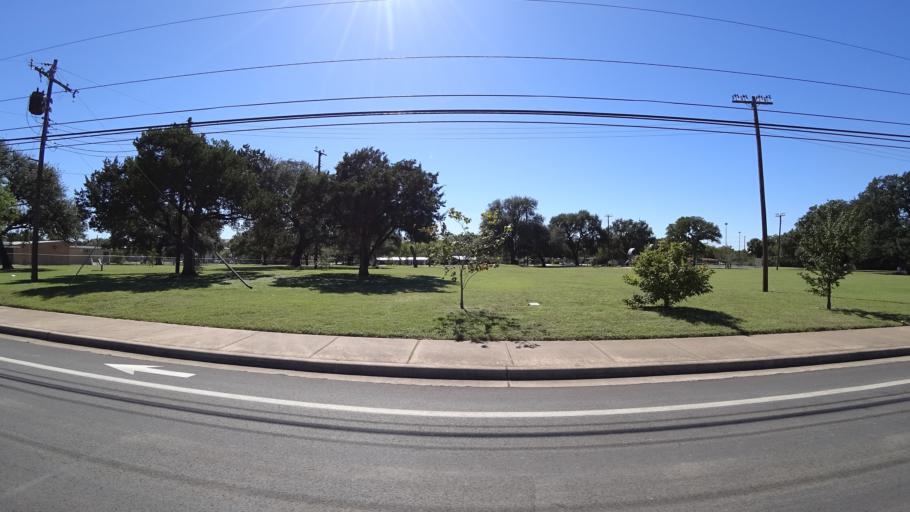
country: US
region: Texas
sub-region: Travis County
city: Rollingwood
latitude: 30.2292
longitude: -97.7913
